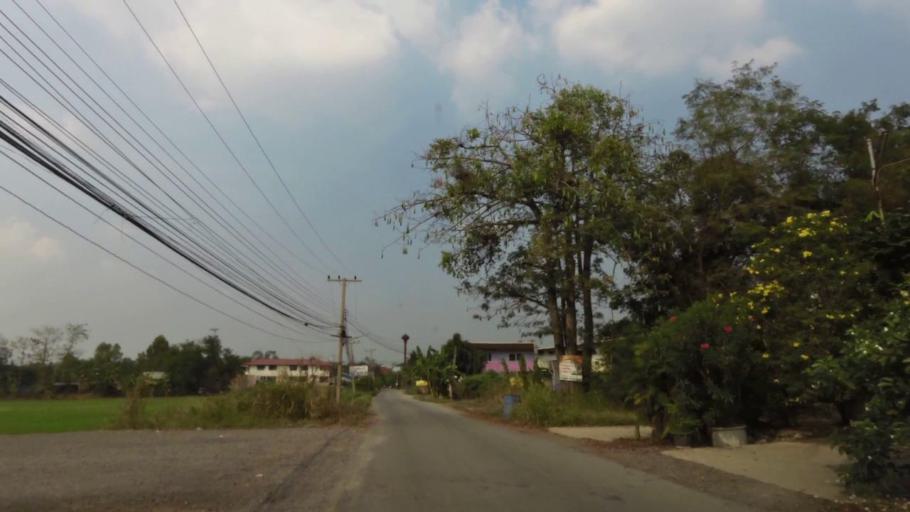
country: TH
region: Phra Nakhon Si Ayutthaya
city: Phra Nakhon Si Ayutthaya
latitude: 14.3066
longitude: 100.5646
